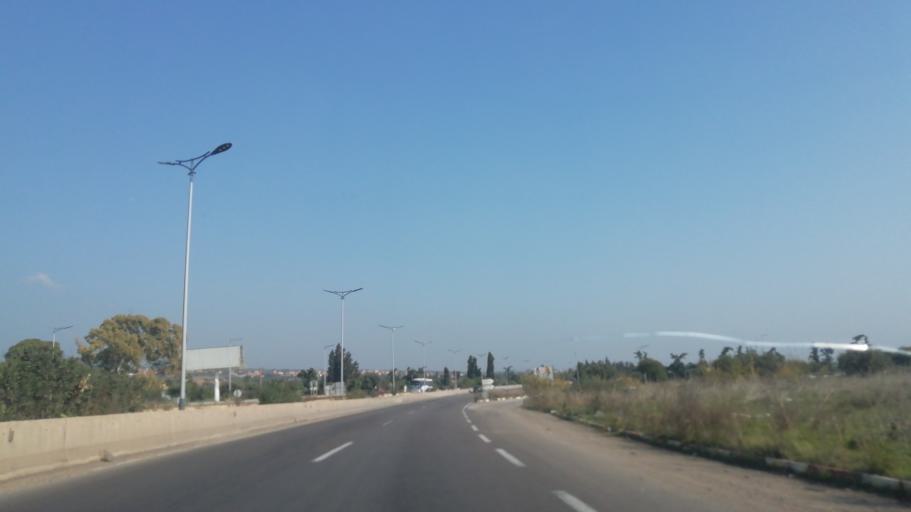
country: DZ
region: Oran
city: Bou Tlelis
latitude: 35.5720
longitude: -0.8811
